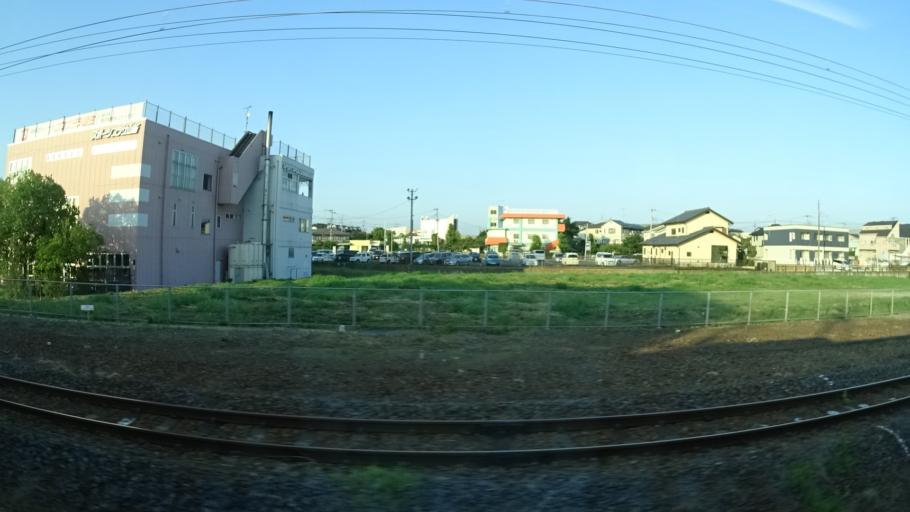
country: JP
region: Ibaraki
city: Ishioka
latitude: 36.1928
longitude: 140.2789
